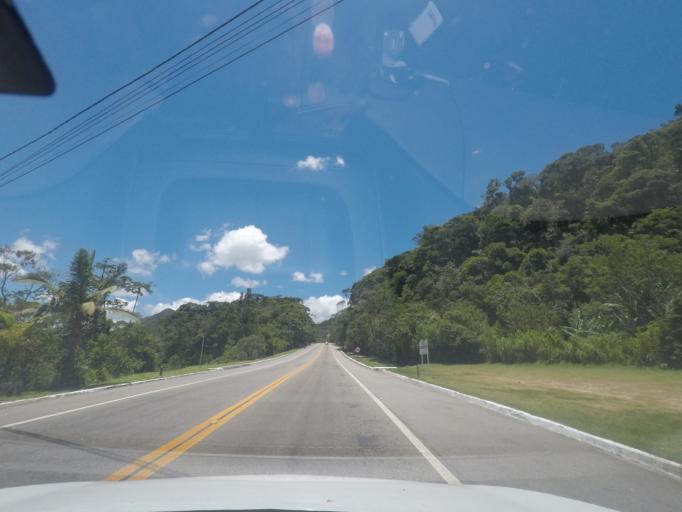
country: BR
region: Rio de Janeiro
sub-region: Teresopolis
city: Teresopolis
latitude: -22.4621
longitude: -42.9852
